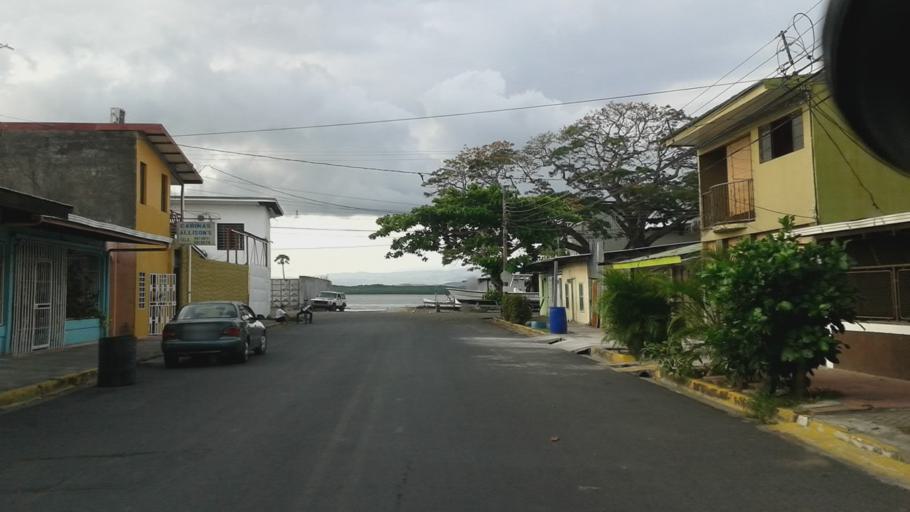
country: CR
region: Puntarenas
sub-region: Canton Central de Puntarenas
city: Puntarenas
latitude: 9.9771
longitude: -84.8470
